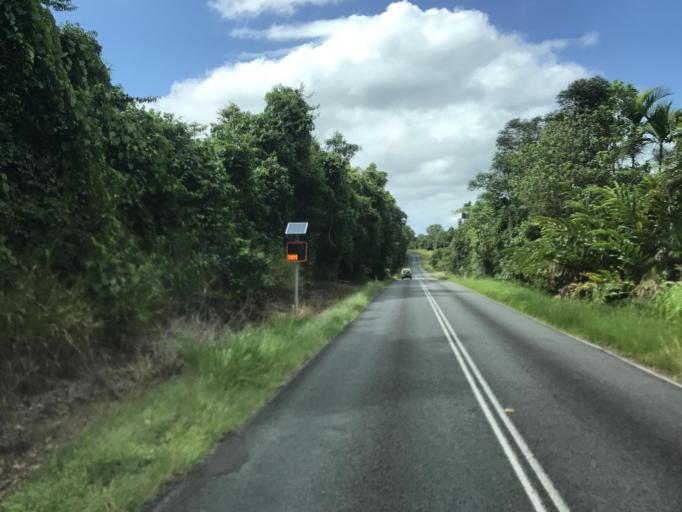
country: AU
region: Queensland
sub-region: Cassowary Coast
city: Innisfail
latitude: -17.8331
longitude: 146.0534
